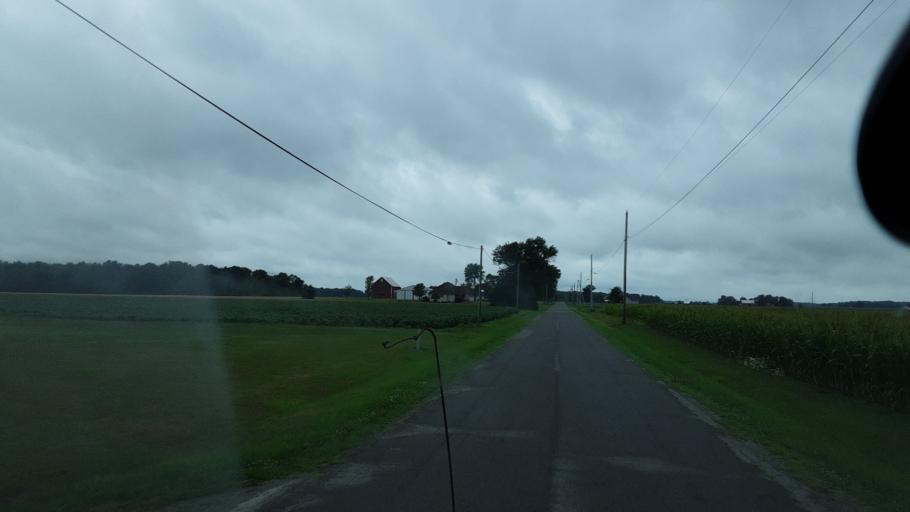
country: US
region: Ohio
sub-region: Van Wert County
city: Convoy
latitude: 40.8224
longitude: -84.7296
